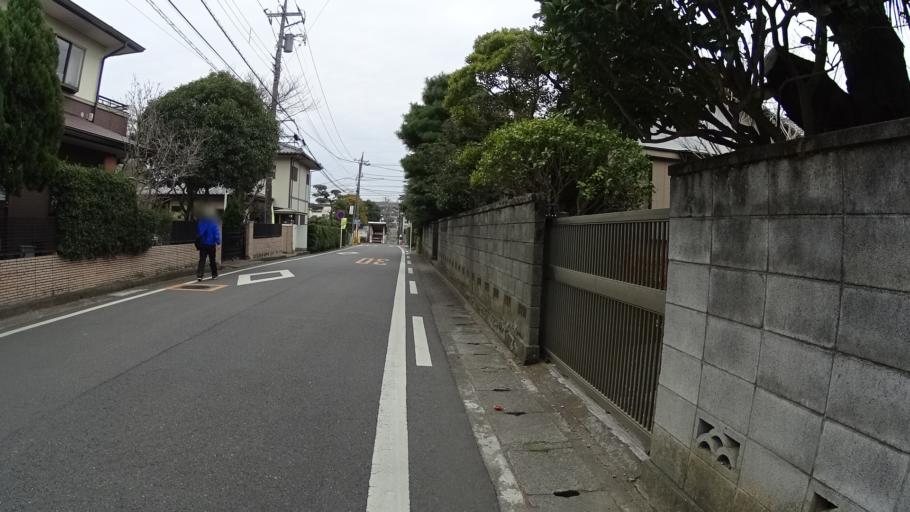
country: JP
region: Kanagawa
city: Oiso
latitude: 35.3102
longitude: 139.3082
